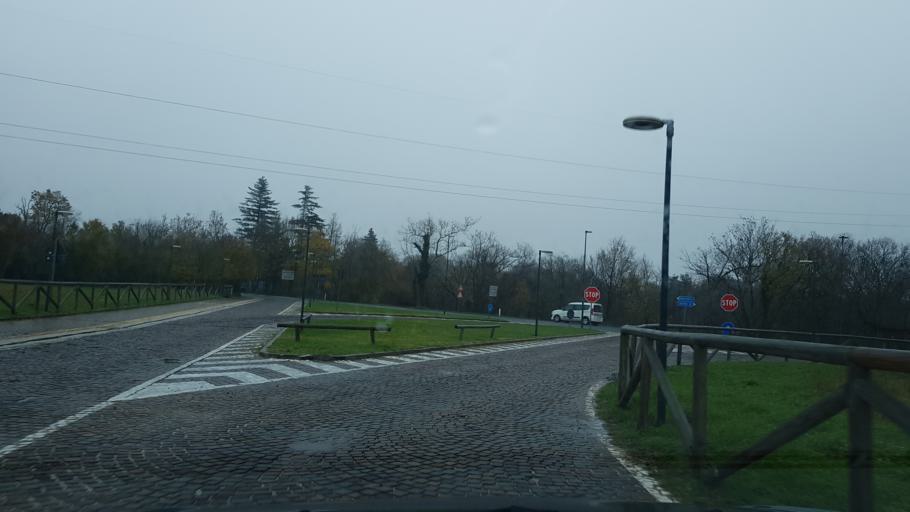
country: IT
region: Friuli Venezia Giulia
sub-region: Provincia di Trieste
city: Domio
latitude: 45.6402
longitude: 13.8545
